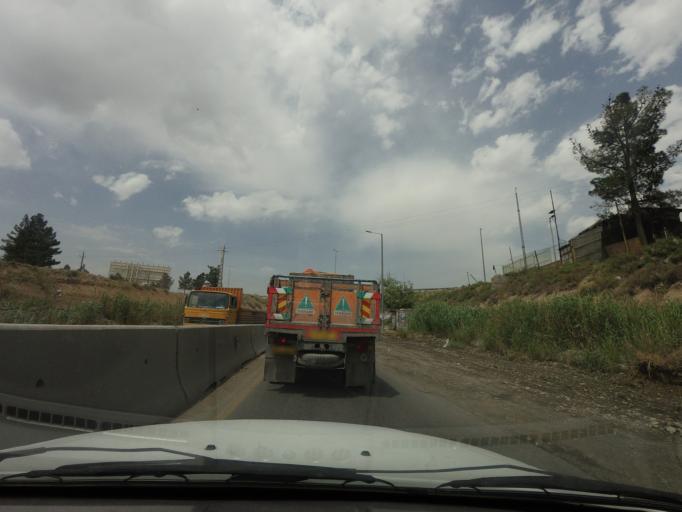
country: IR
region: Tehran
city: Shahrak-e Emam Hasan-e Mojtaba
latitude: 35.5086
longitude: 51.2942
